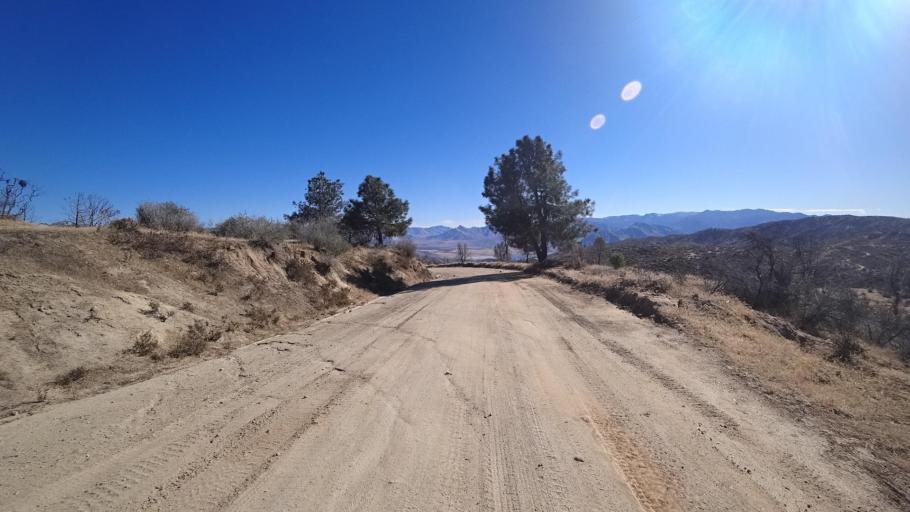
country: US
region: California
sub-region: Kern County
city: Alta Sierra
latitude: 35.7150
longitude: -118.5183
